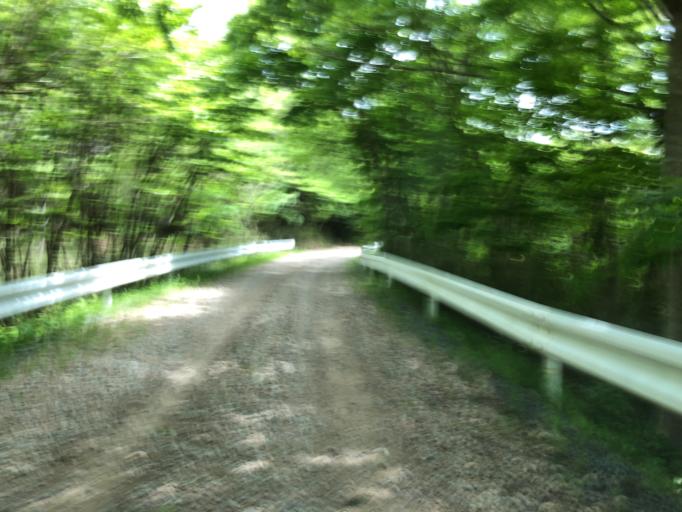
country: JP
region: Miyagi
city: Marumori
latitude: 37.7344
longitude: 140.8303
